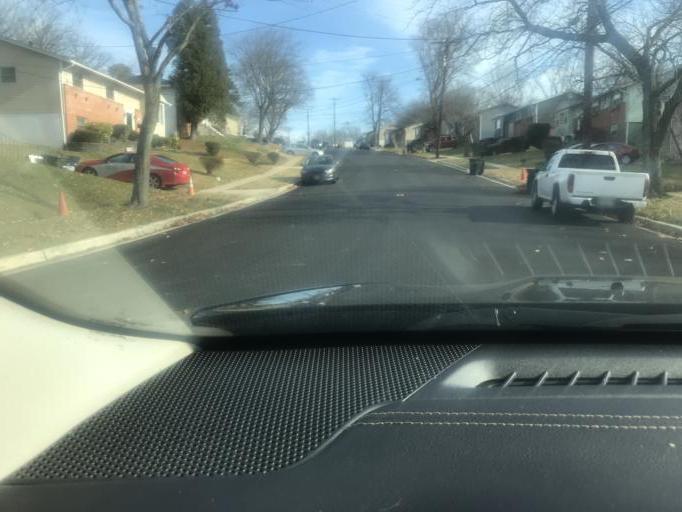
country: US
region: Maryland
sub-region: Prince George's County
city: Oxon Hill
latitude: 38.8080
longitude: -76.9831
